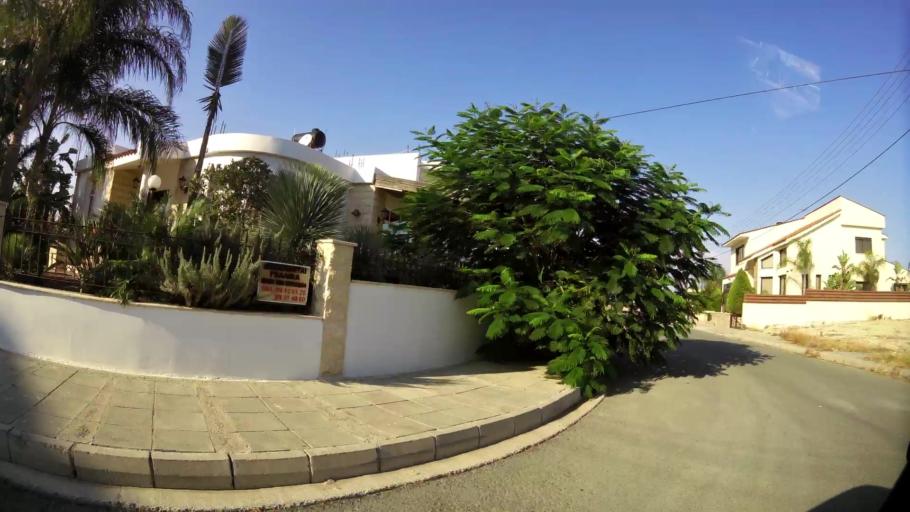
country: CY
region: Larnaka
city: Aradippou
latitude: 34.9418
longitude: 33.6012
